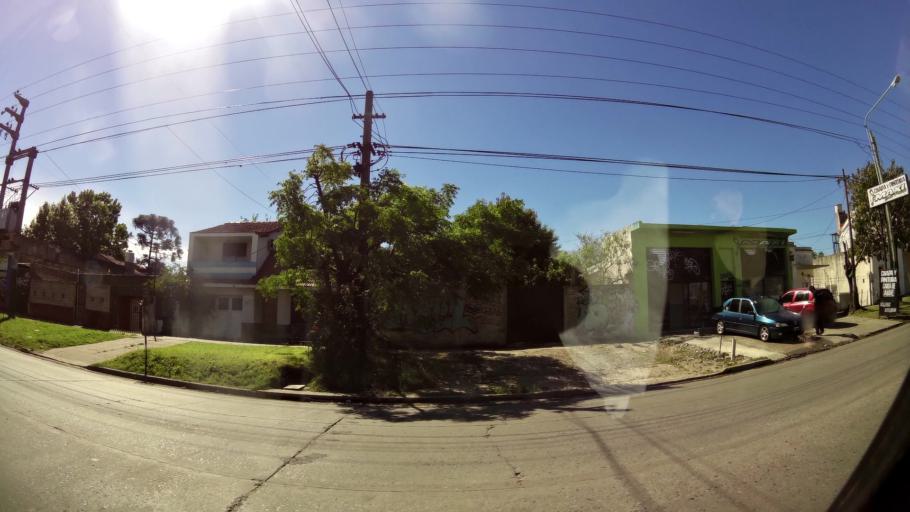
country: AR
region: Buenos Aires
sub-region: Partido de Almirante Brown
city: Adrogue
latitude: -34.7964
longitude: -58.3654
